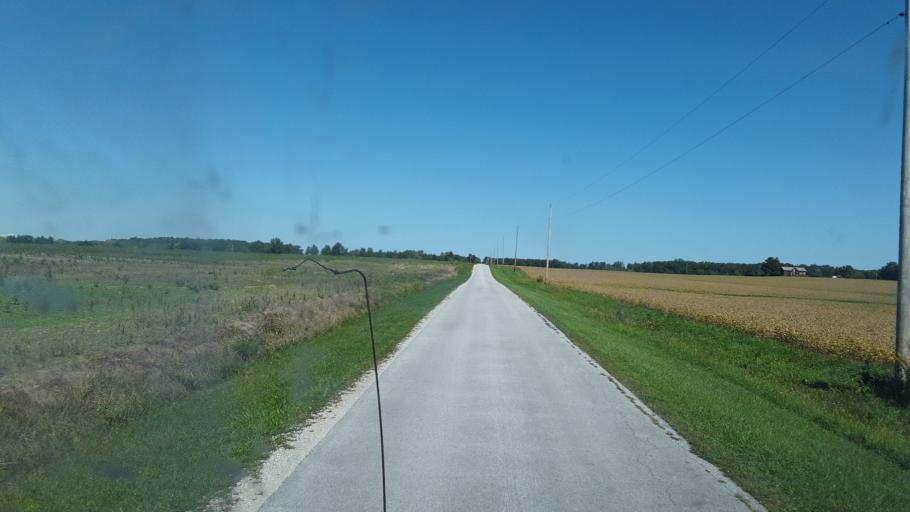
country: US
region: Ohio
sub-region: Sandusky County
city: Mount Carmel
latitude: 41.1412
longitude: -82.9575
